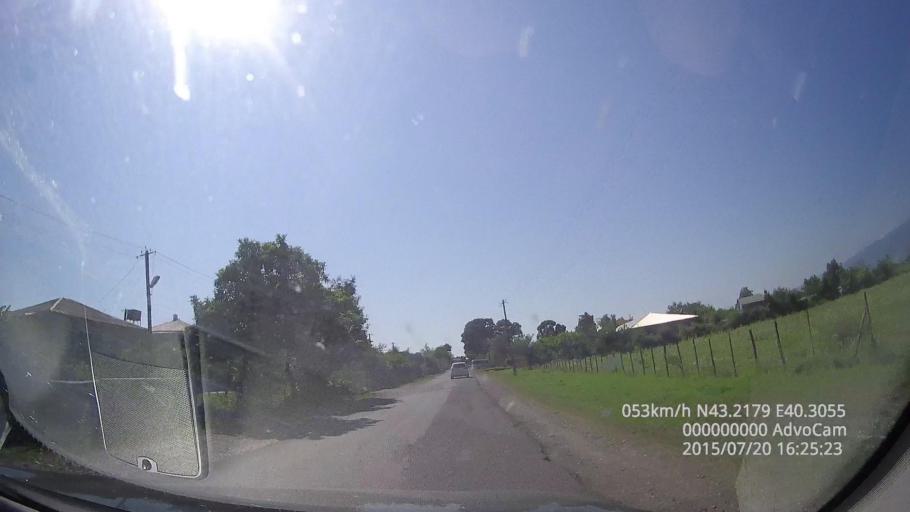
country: GE
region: Abkhazia
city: Bich'vinta
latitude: 43.2179
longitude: 40.3055
